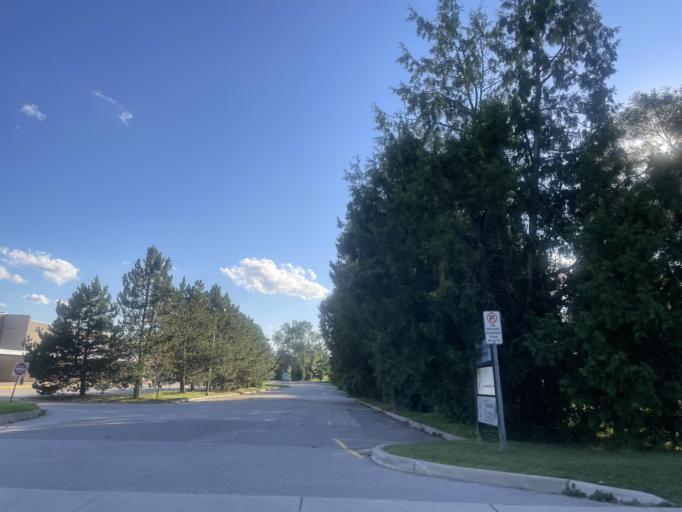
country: CA
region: Ontario
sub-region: Wellington County
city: Guelph
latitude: 43.5489
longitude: -80.2681
